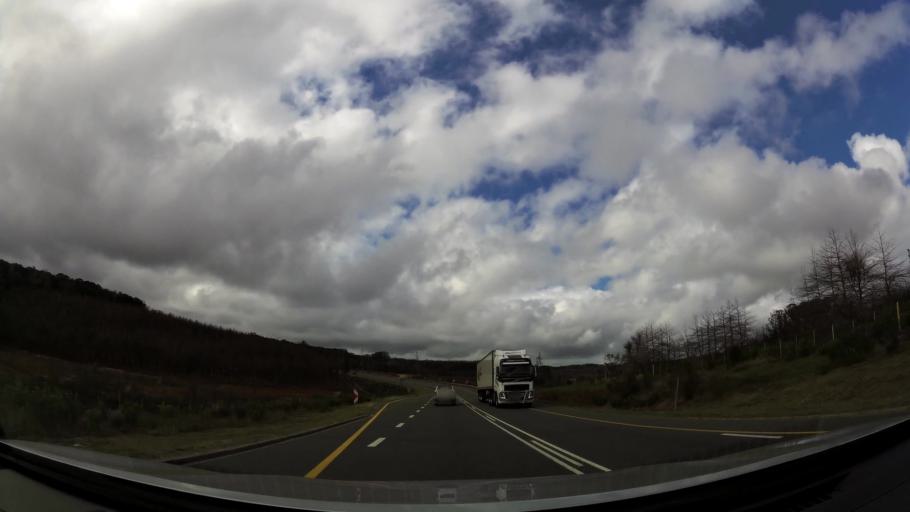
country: ZA
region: Western Cape
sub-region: Eden District Municipality
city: Knysna
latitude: -34.0362
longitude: 23.1545
